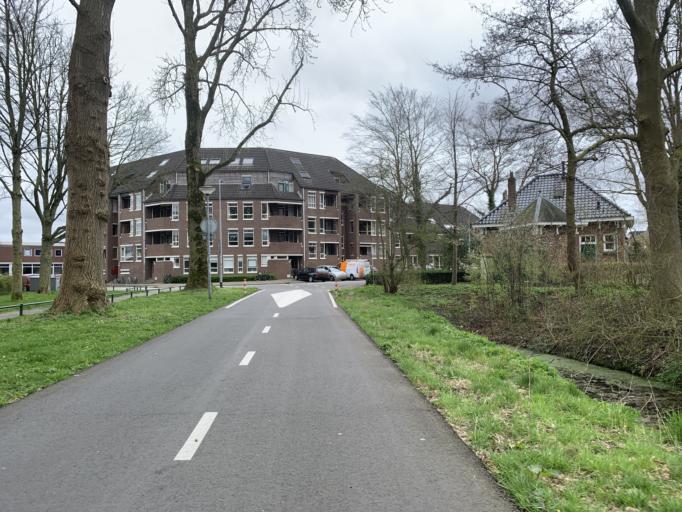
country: NL
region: Groningen
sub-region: Gemeente Groningen
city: Korrewegwijk
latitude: 53.2310
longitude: 6.5518
